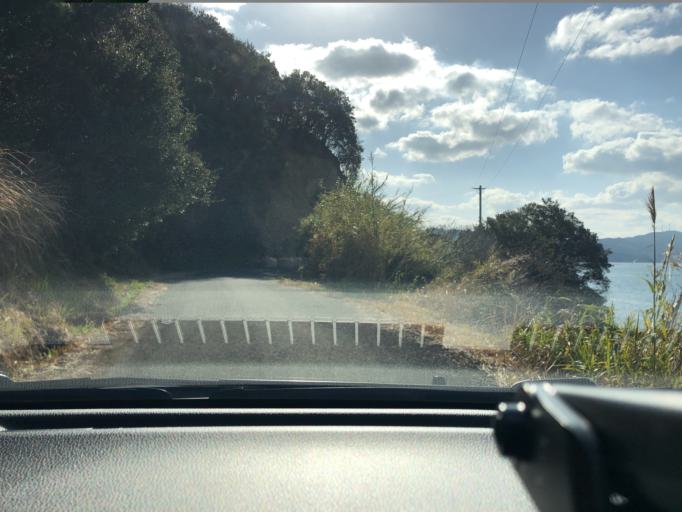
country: JP
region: Kochi
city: Sukumo
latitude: 32.9136
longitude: 132.6892
